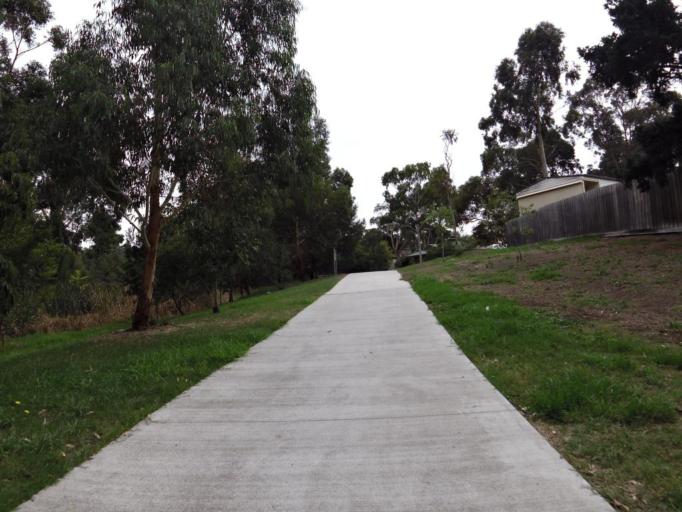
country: AU
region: Victoria
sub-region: Hume
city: Sunbury
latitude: -37.5703
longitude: 144.7286
